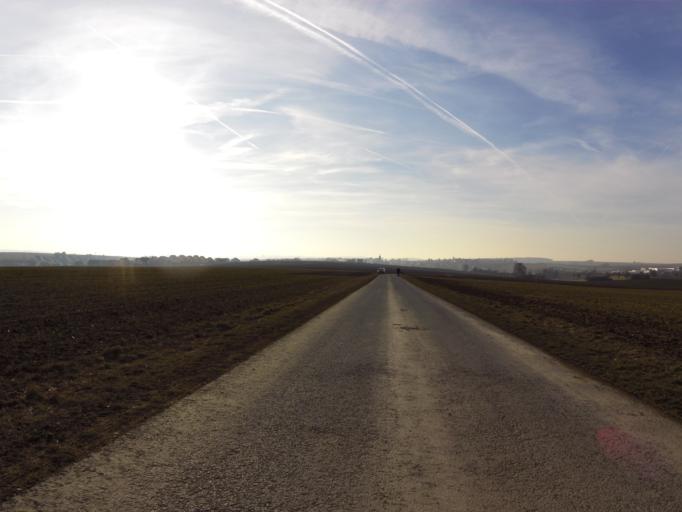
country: DE
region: Bavaria
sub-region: Regierungsbezirk Unterfranken
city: Kurnach
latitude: 49.8316
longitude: 10.0267
